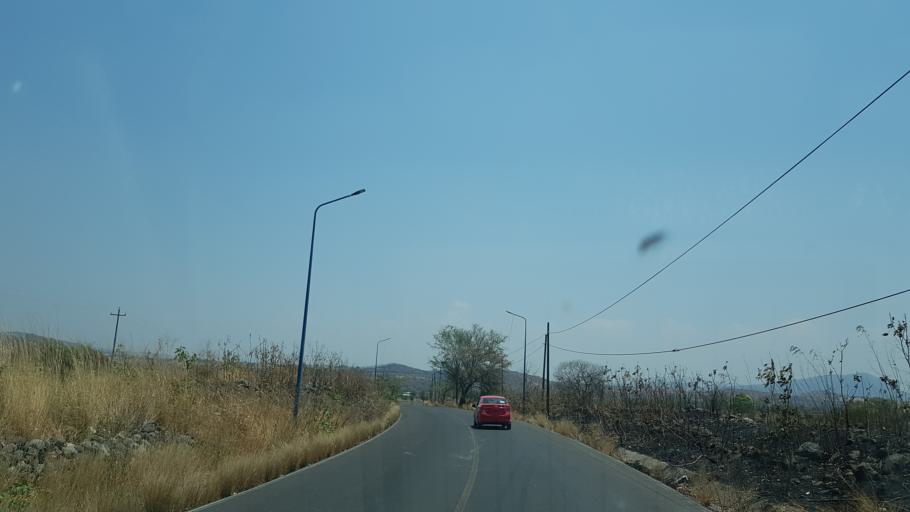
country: MX
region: Puebla
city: Huaquechula
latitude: 18.7663
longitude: -98.5328
